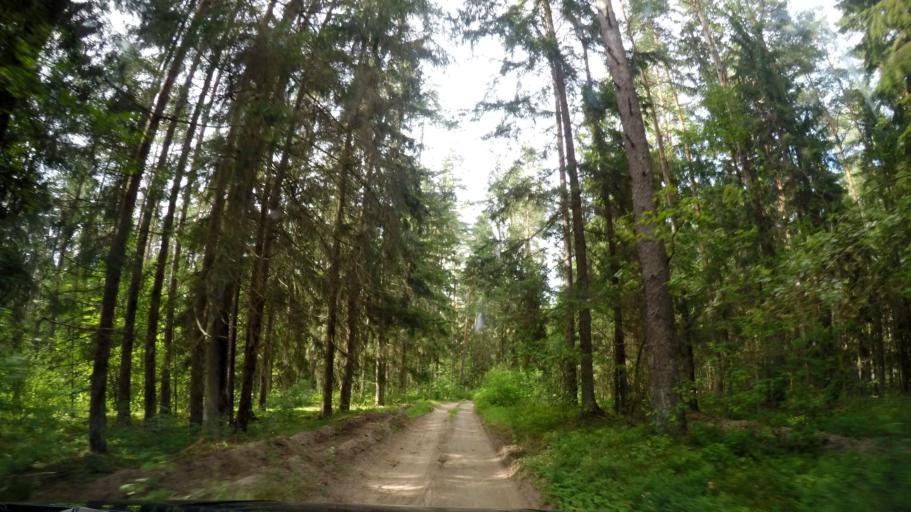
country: BY
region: Grodnenskaya
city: Skidal'
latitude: 53.8311
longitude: 24.1775
